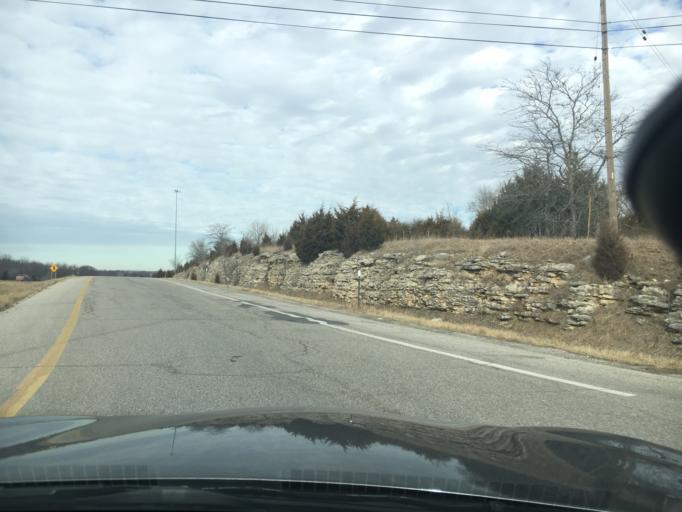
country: US
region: Missouri
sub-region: Cass County
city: Belton
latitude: 38.8037
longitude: -94.6747
